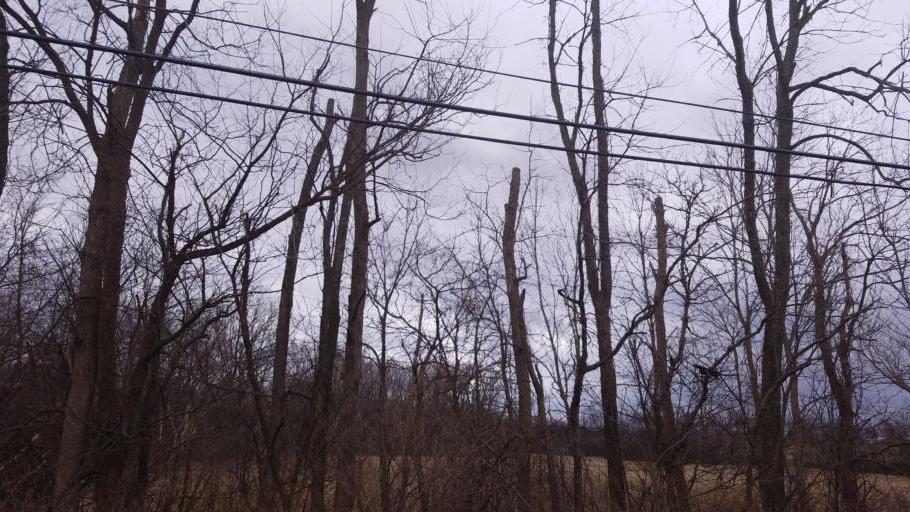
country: US
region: Ohio
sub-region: Knox County
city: Fredericktown
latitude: 40.4744
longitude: -82.6842
